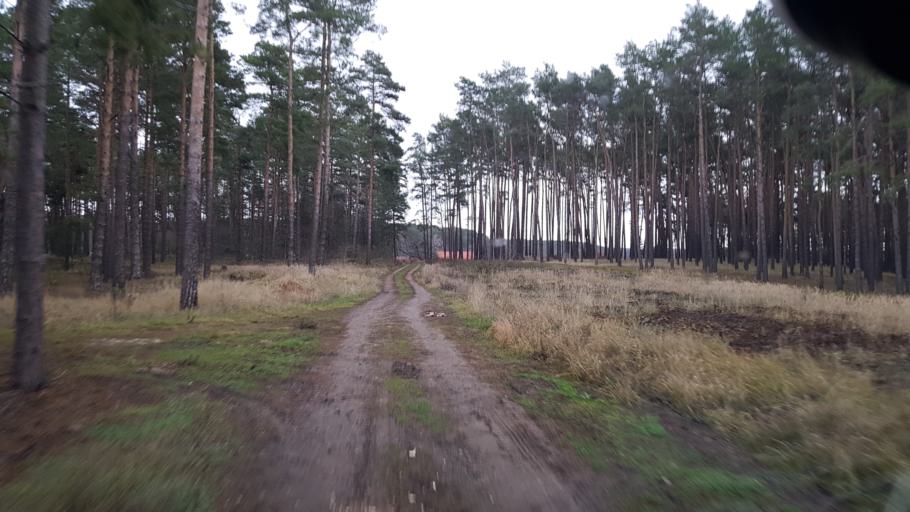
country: DE
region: Brandenburg
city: Hohenbucko
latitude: 51.7424
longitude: 13.4342
